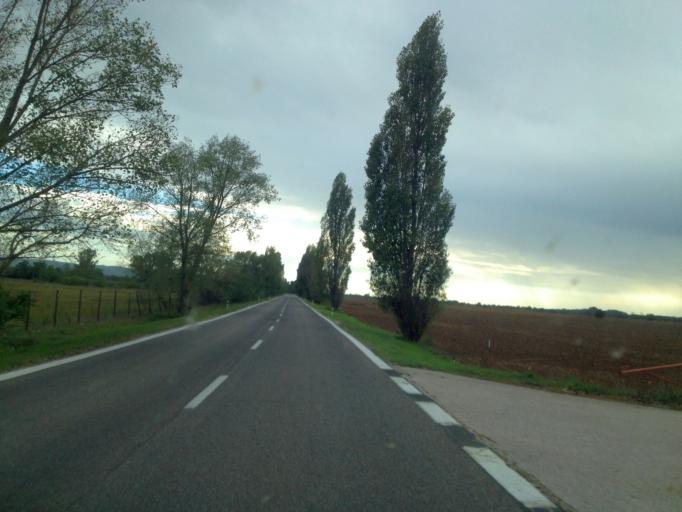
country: HU
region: Komarom-Esztergom
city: Sutto
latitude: 47.7775
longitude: 18.4448
